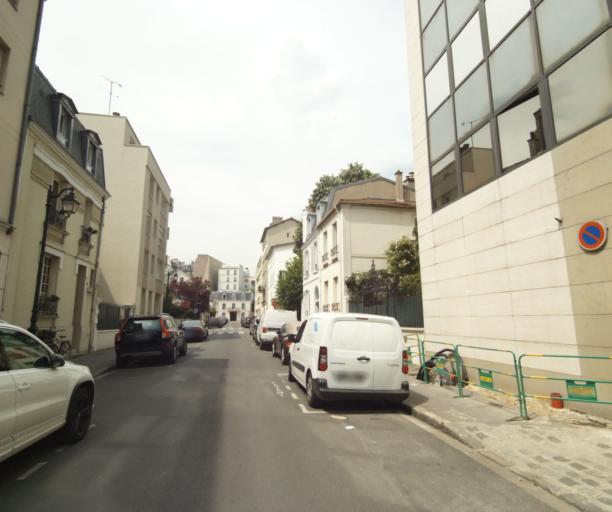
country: FR
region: Ile-de-France
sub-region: Departement des Hauts-de-Seine
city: Asnieres-sur-Seine
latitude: 48.9080
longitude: 2.2919
